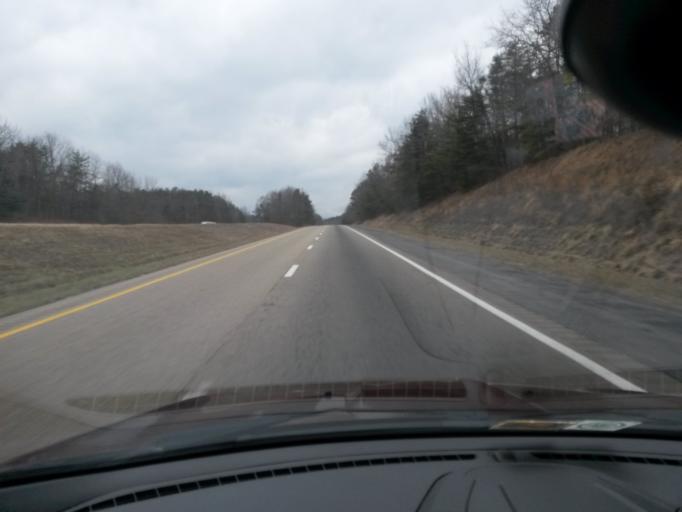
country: US
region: Virginia
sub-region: Alleghany County
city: Clifton Forge
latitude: 37.8232
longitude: -79.7462
